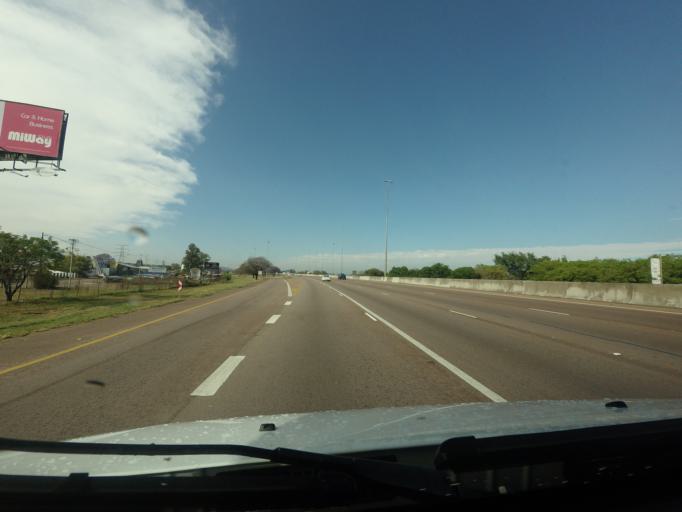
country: ZA
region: Gauteng
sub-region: City of Tshwane Metropolitan Municipality
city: Pretoria
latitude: -25.7074
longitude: 28.2671
